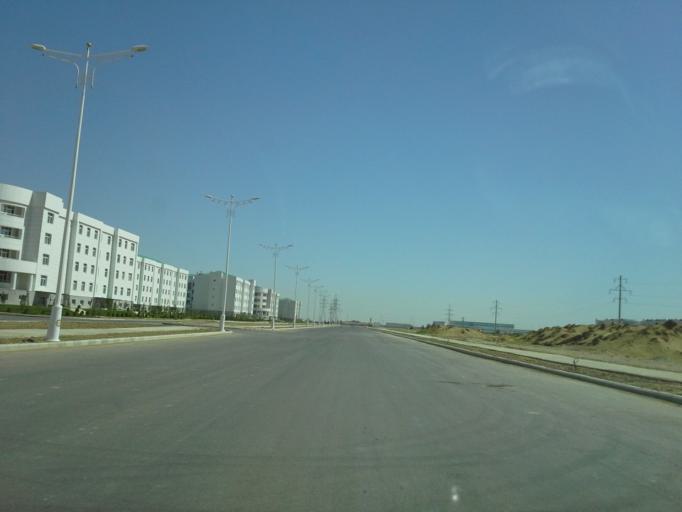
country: TM
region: Ahal
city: Ashgabat
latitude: 37.9754
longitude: 58.3326
